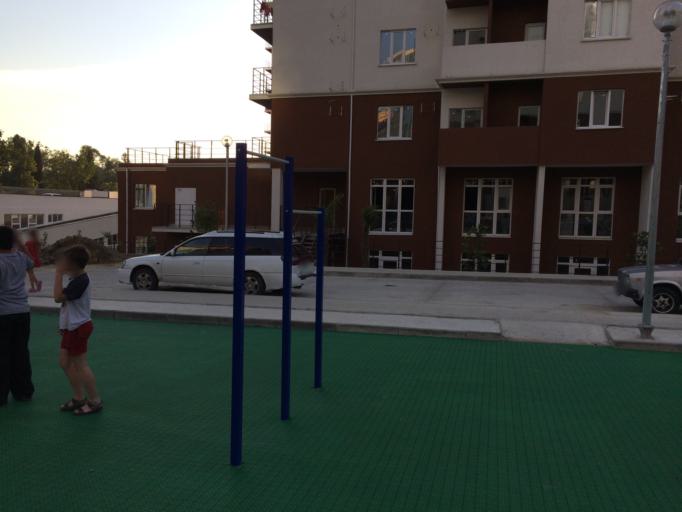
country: RU
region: Krasnodarskiy
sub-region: Sochi City
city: Sochi
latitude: 43.5906
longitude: 39.7335
